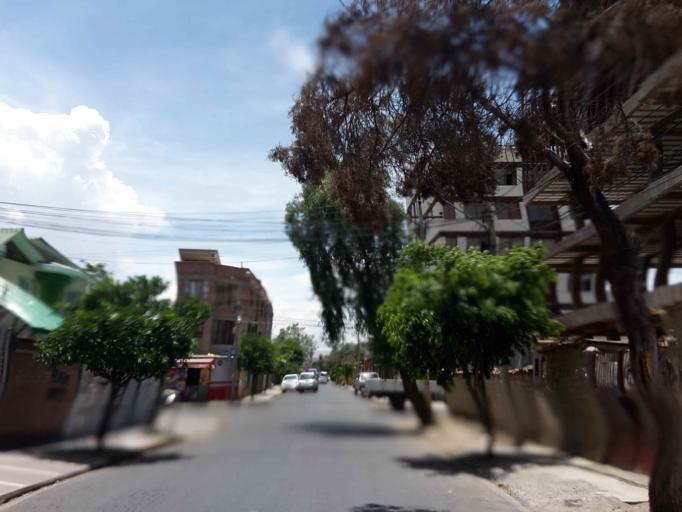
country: BO
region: Cochabamba
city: Cochabamba
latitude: -17.3788
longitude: -66.1829
